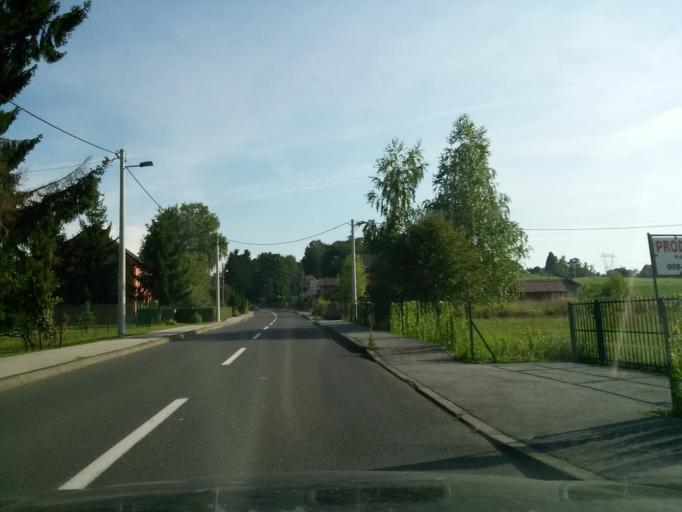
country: HR
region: Grad Zagreb
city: Strmec
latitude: 45.6777
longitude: 15.8748
